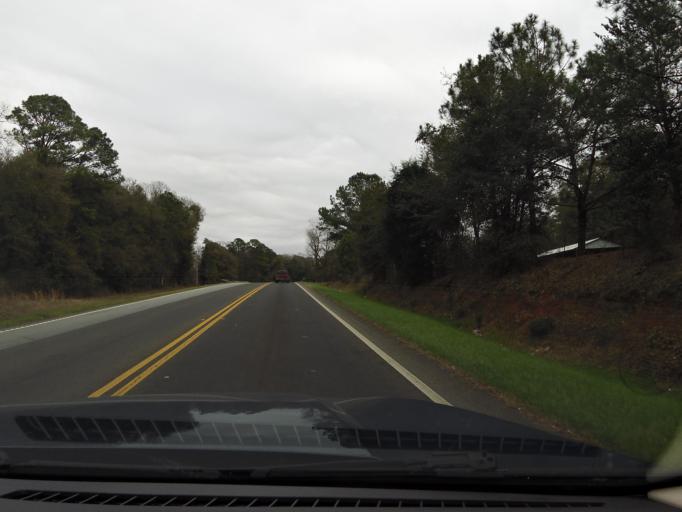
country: US
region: Georgia
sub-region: Randolph County
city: Shellman
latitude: 31.7822
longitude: -84.5969
